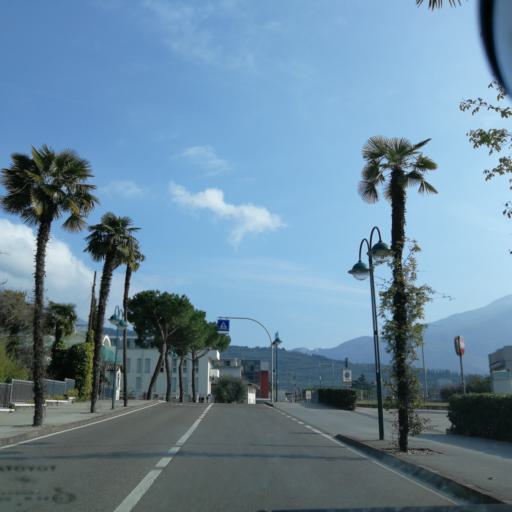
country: IT
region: Trentino-Alto Adige
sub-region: Provincia di Trento
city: Riva del Garda
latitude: 45.8854
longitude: 10.8477
